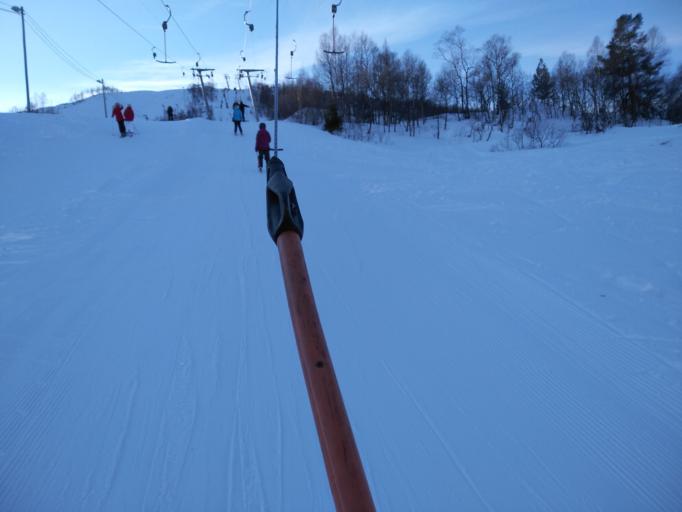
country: NO
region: Rogaland
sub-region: Sauda
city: Sauda
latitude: 59.6215
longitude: 6.2389
